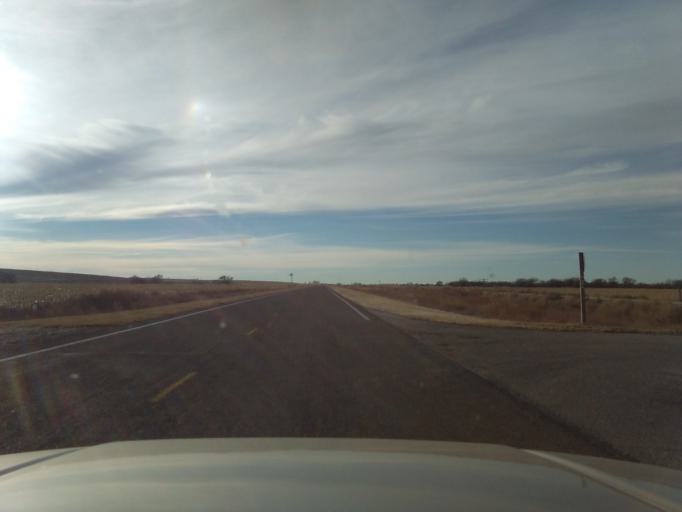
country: US
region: Kansas
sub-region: Norton County
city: Norton
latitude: 39.7559
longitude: -100.1195
